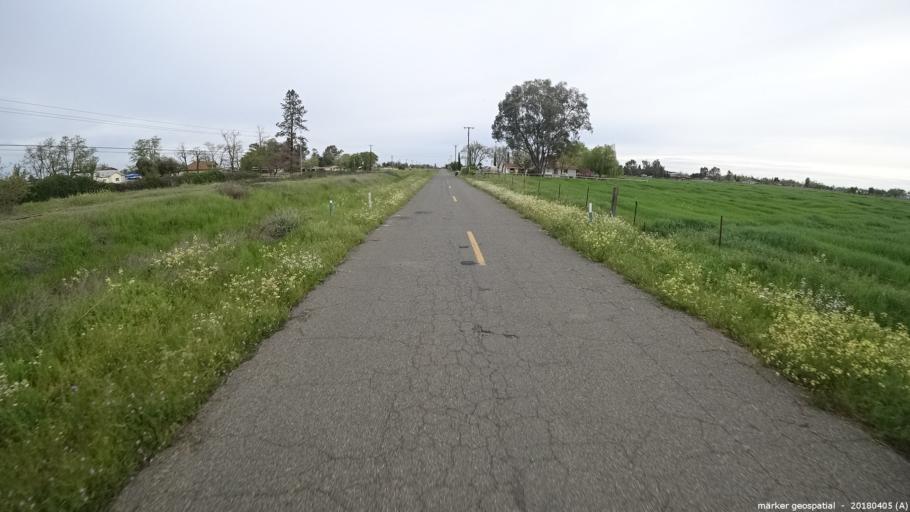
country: US
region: California
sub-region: Sacramento County
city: Herald
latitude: 38.2816
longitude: -121.2445
